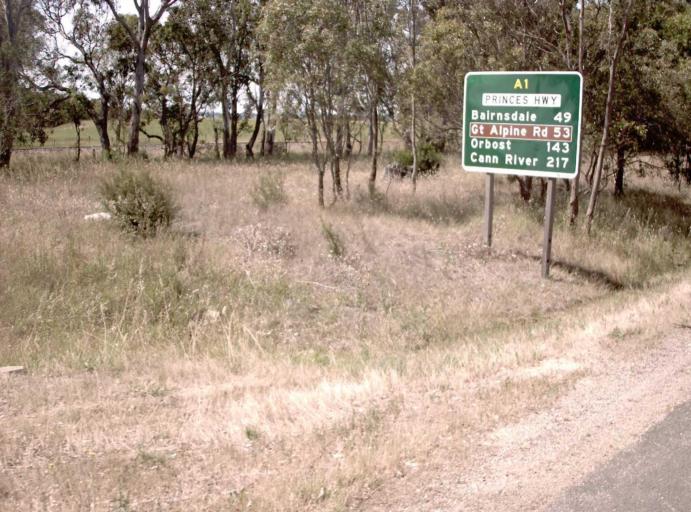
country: AU
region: Victoria
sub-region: Wellington
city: Sale
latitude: -37.9539
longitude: 147.1045
